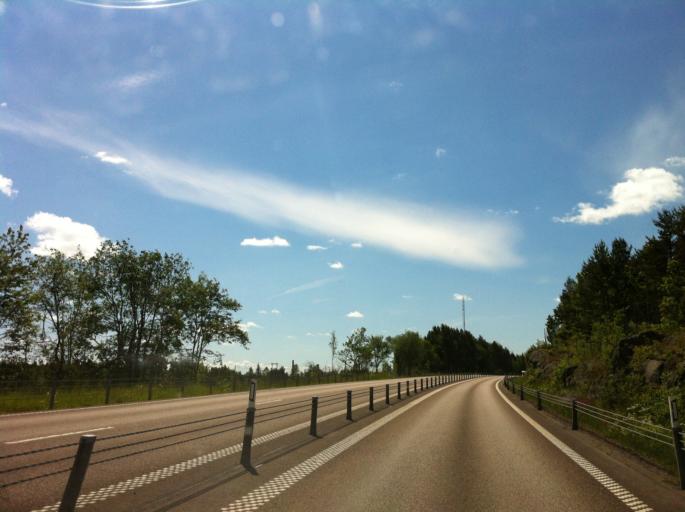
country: SE
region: Vaestra Goetaland
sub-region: Melleruds Kommun
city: Mellerud
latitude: 58.8056
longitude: 12.5263
